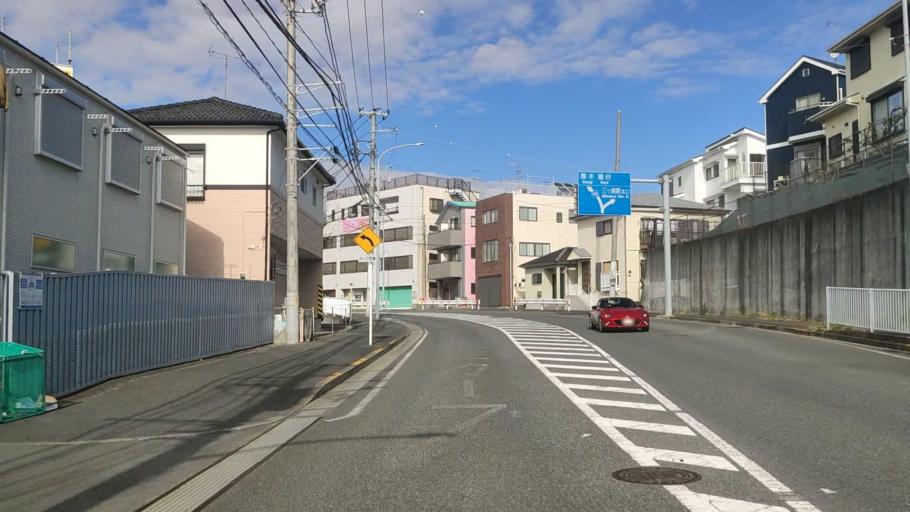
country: JP
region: Kanagawa
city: Minami-rinkan
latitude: 35.4665
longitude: 139.5073
